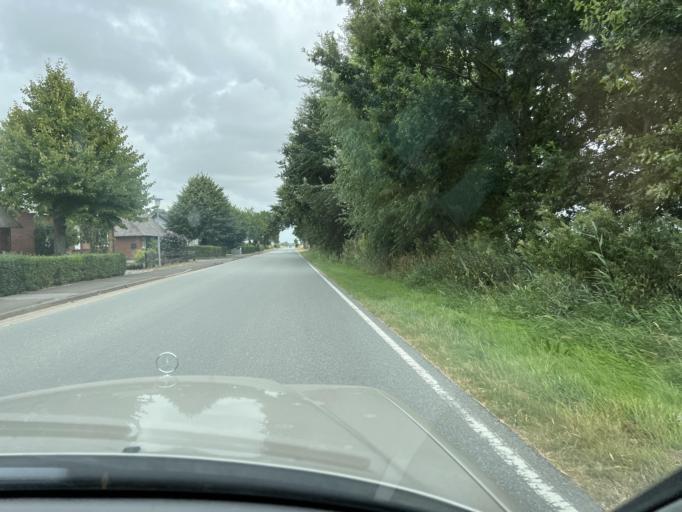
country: DE
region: Schleswig-Holstein
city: Hemme
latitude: 54.2828
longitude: 9.0146
